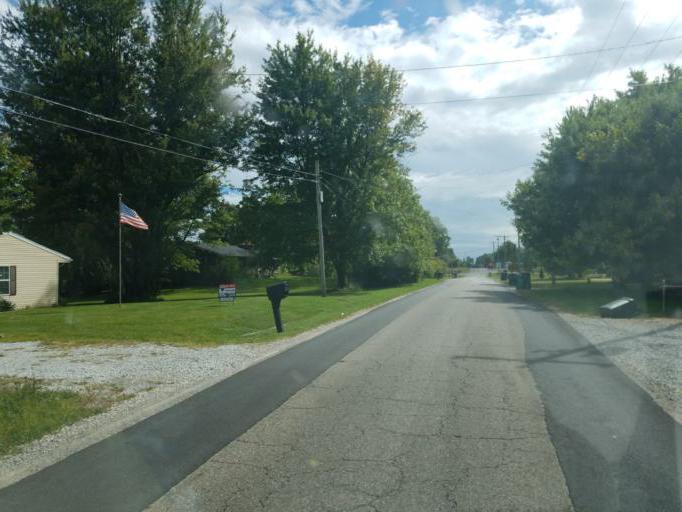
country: US
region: Ohio
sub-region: Licking County
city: Pataskala
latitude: 39.9994
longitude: -82.7289
